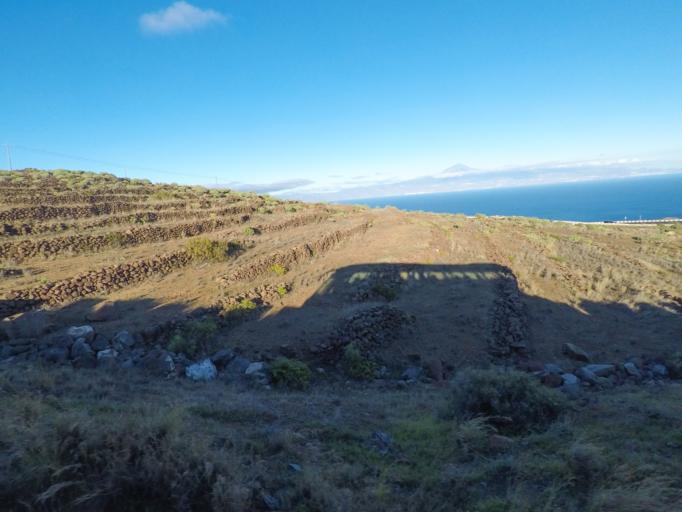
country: ES
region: Canary Islands
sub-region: Provincia de Santa Cruz de Tenerife
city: San Sebastian de la Gomera
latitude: 28.0853
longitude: -17.1448
